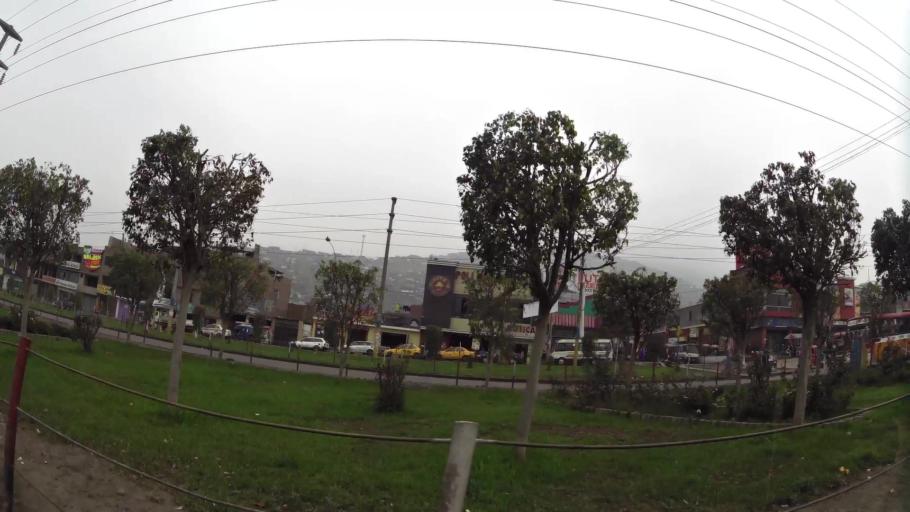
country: PE
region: Lima
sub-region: Lima
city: Urb. Santo Domingo
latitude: -11.9334
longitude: -76.9689
